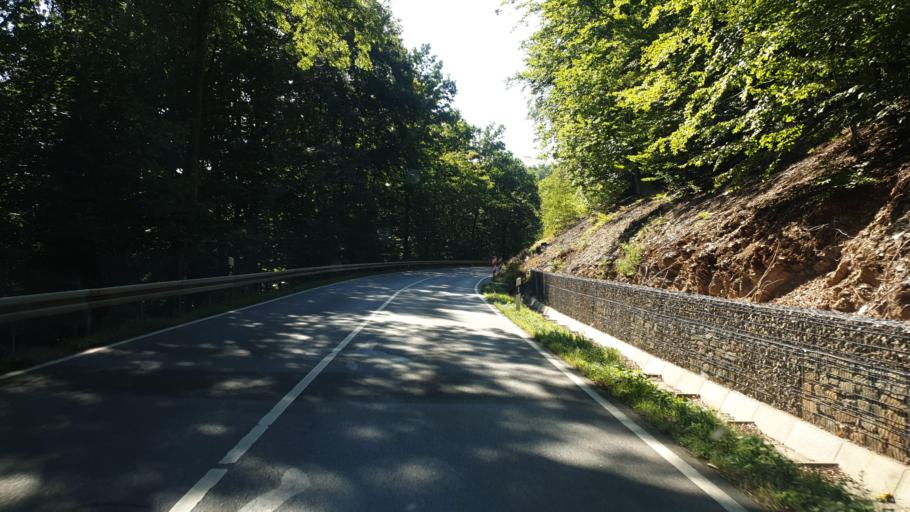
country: DE
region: Saxony
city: Lauter
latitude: 50.5878
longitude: 12.7360
